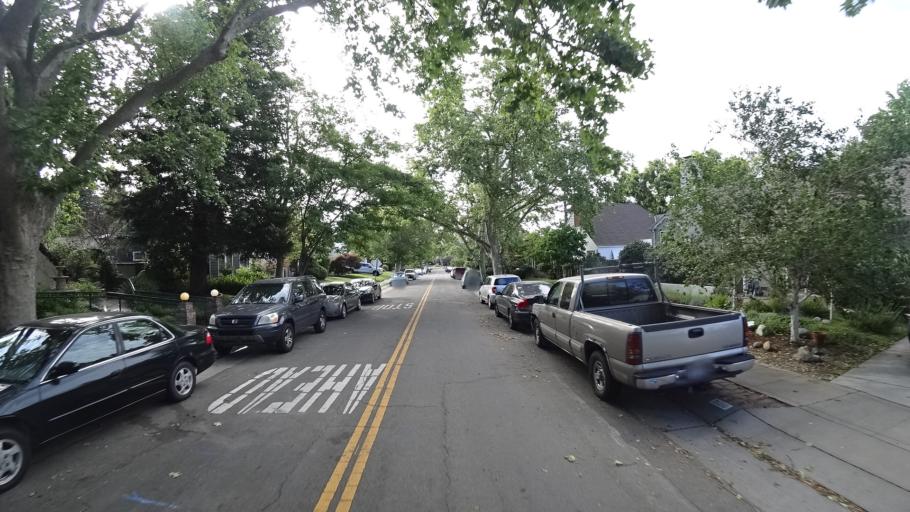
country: US
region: California
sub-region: Sacramento County
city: Sacramento
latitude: 38.5584
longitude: -121.5047
